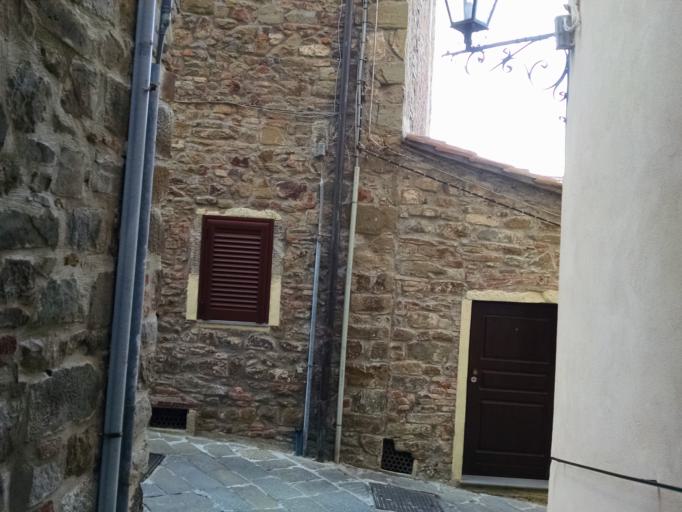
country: IT
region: Tuscany
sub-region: Provincia di Grosseto
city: Scarlino
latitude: 42.9076
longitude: 10.8519
